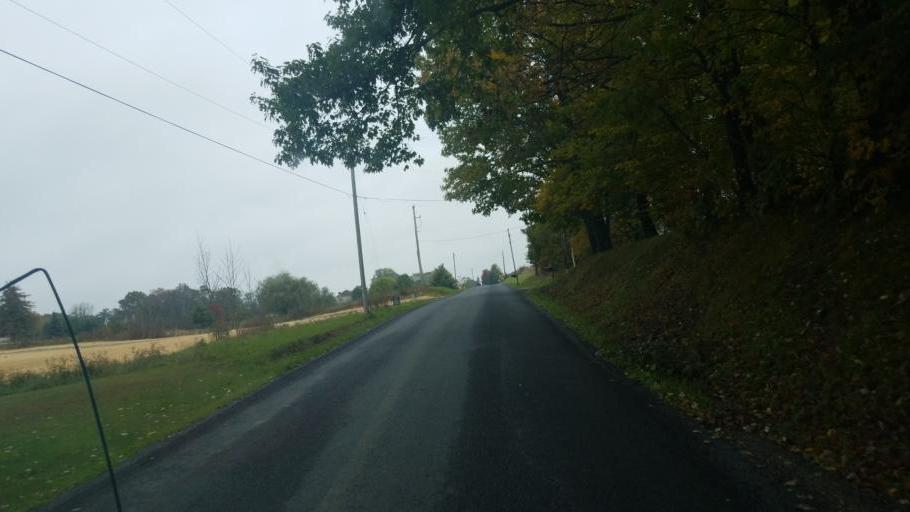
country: US
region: Ohio
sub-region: Richland County
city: Ontario
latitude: 40.7331
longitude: -82.6572
